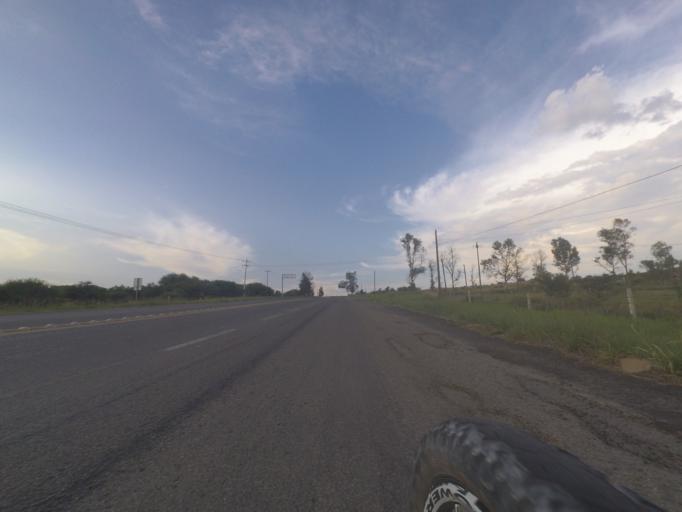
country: MX
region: Aguascalientes
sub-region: Aguascalientes
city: La Loma de los Negritos
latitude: 21.8375
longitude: -102.3762
